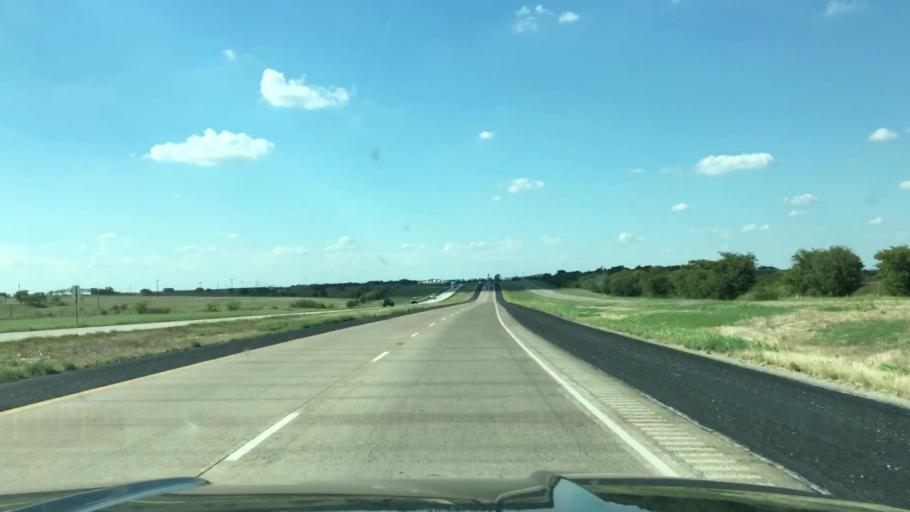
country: US
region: Texas
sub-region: Wise County
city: New Fairview
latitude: 33.1116
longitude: -97.4779
